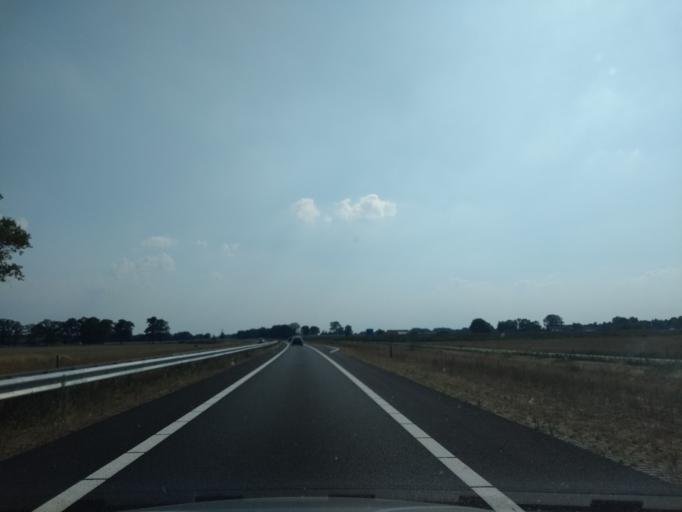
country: NL
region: Overijssel
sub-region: Gemeente Haaksbergen
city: Haaksbergen
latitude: 52.1556
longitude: 6.6882
